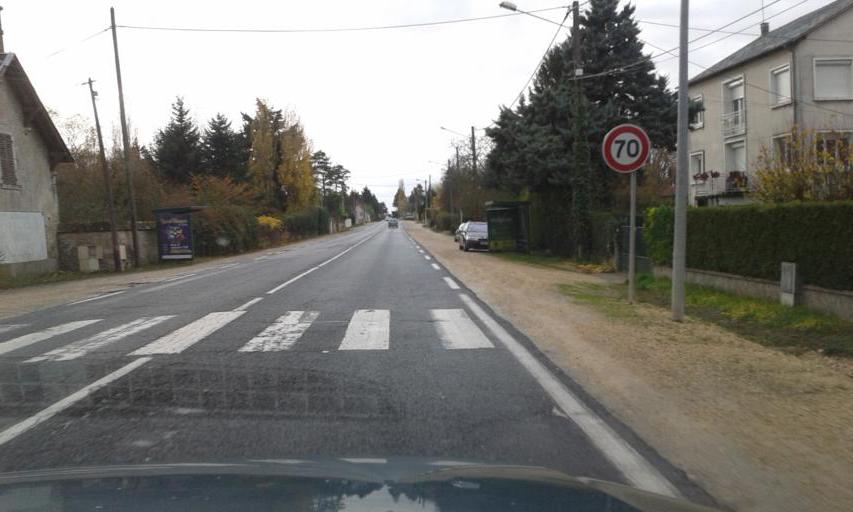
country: FR
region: Centre
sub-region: Departement du Loiret
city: Mareau-aux-Pres
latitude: 47.8670
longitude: 1.7754
